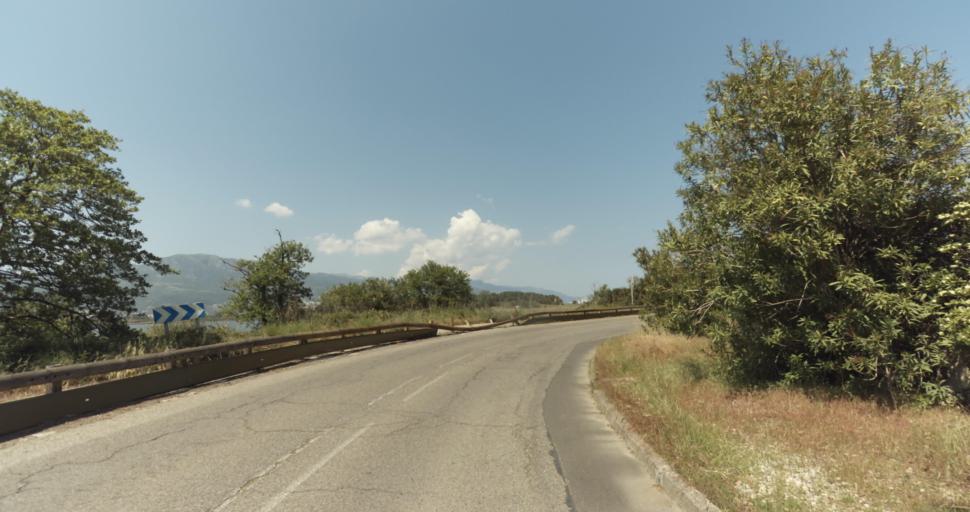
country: FR
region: Corsica
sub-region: Departement de la Haute-Corse
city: Biguglia
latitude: 42.6397
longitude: 9.4591
